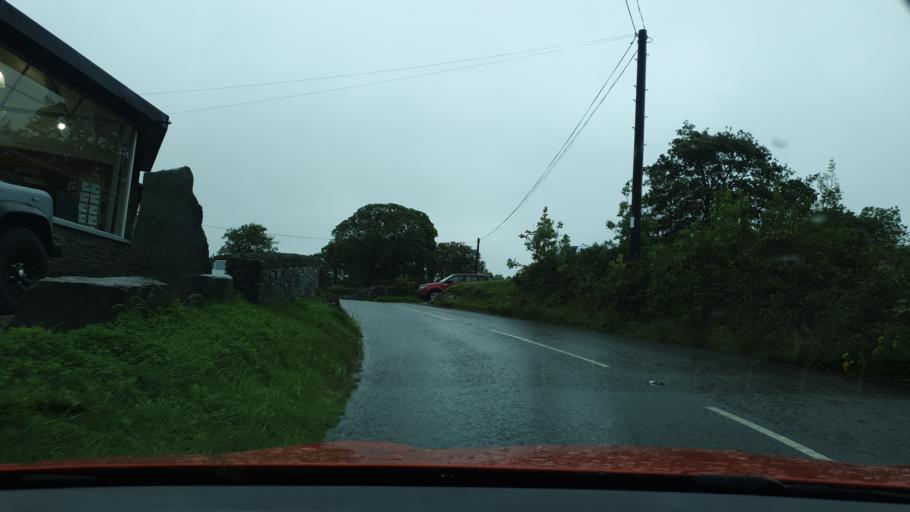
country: GB
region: England
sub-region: Cumbria
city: Ulverston
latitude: 54.3290
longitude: -3.0976
